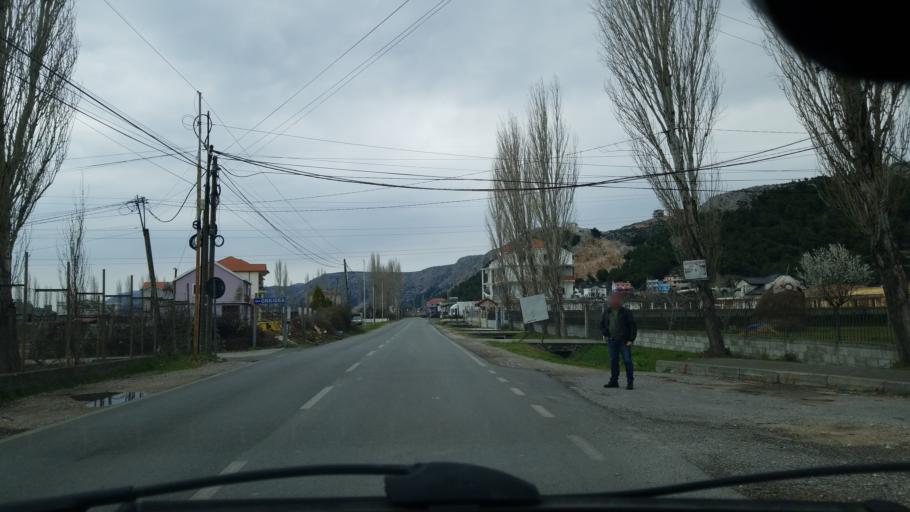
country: AL
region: Lezhe
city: Lezhe
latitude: 41.7839
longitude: 19.6293
